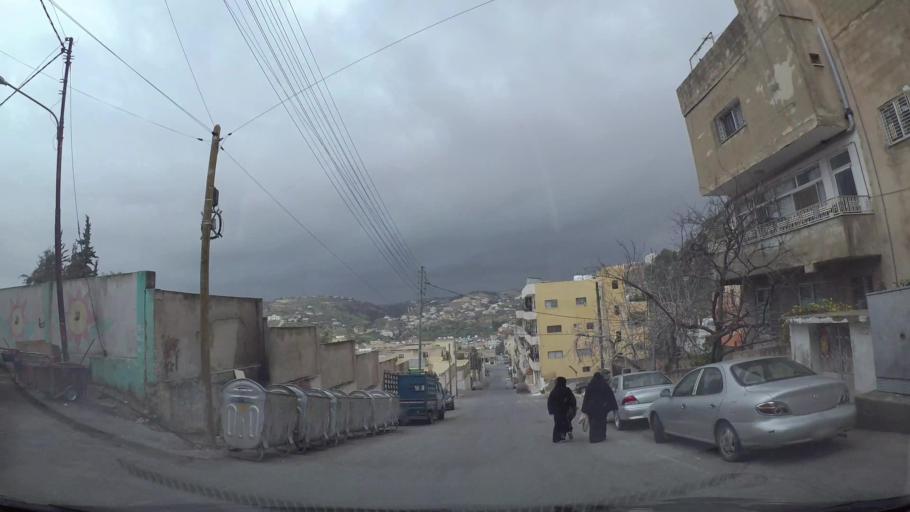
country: JO
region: Amman
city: Wadi as Sir
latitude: 31.9540
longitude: 35.8224
